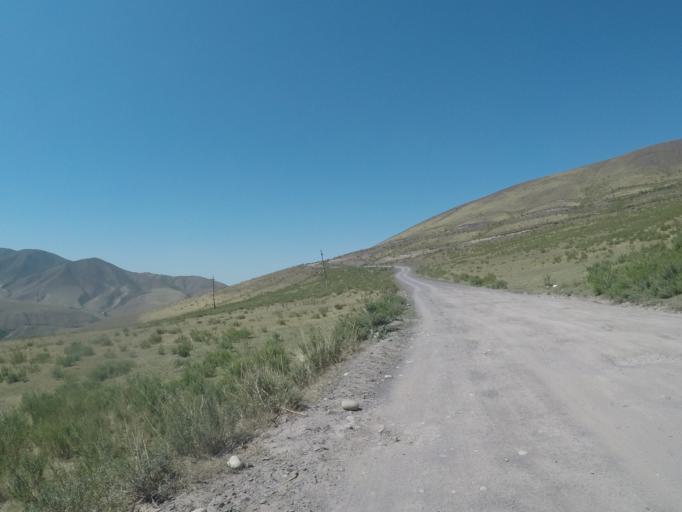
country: KG
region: Chuy
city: Bishkek
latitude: 42.6495
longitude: 74.5175
